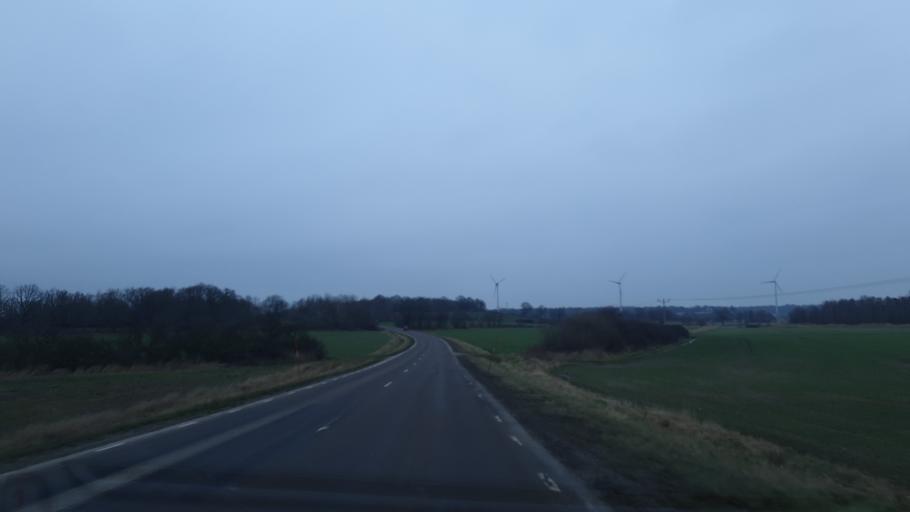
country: SE
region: Blekinge
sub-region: Karlskrona Kommun
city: Jaemjoe
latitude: 56.1544
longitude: 15.7630
